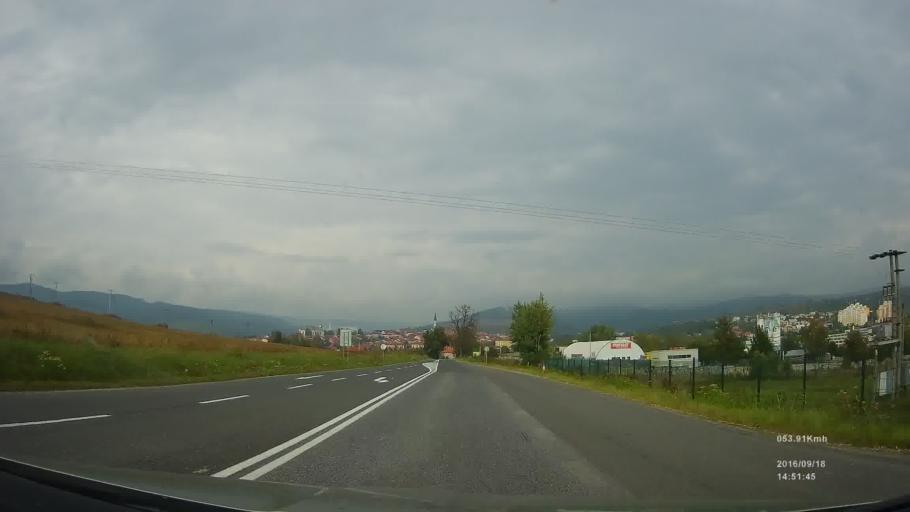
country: SK
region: Presovsky
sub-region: Okres Presov
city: Levoca
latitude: 49.0120
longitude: 20.5862
